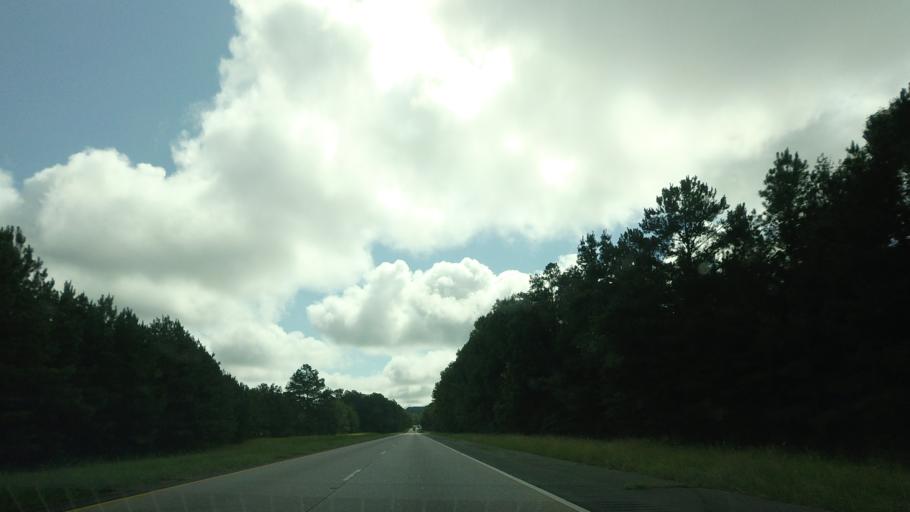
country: US
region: Georgia
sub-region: Twiggs County
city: Jeffersonville
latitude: 32.6500
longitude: -83.4238
